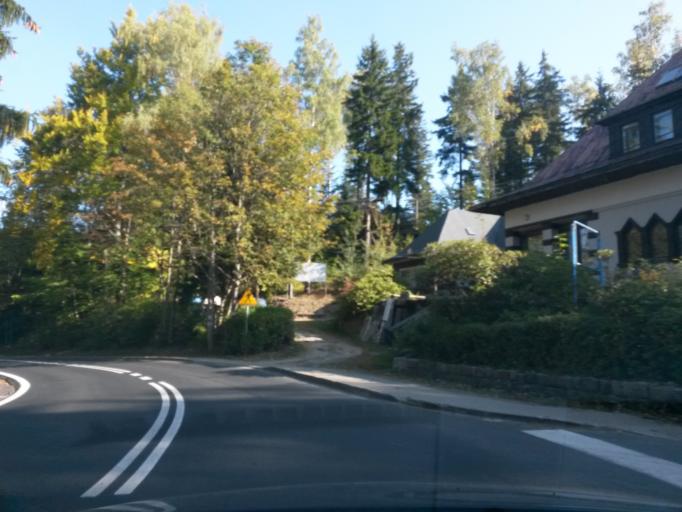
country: PL
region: Lower Silesian Voivodeship
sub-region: Powiat jeleniogorski
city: Szklarska Poreba
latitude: 50.8251
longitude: 15.5071
